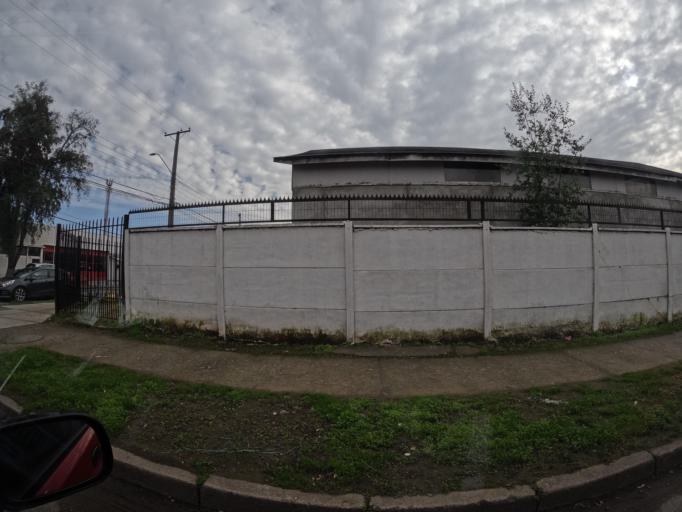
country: CL
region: Maule
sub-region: Provincia de Linares
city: Linares
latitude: -35.8513
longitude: -71.5850
